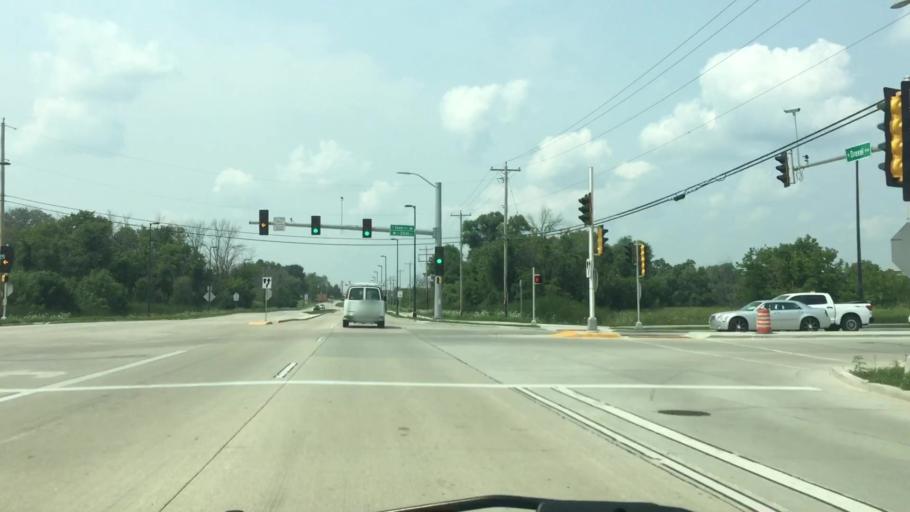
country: US
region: Wisconsin
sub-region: Milwaukee County
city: Greendale
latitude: 42.9017
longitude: -87.9408
